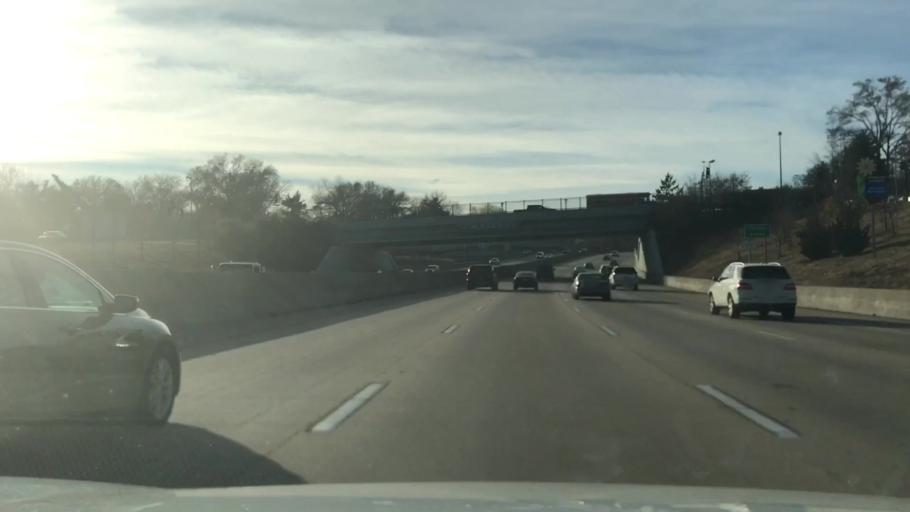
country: US
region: Missouri
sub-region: Saint Louis County
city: Brentwood
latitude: 38.6307
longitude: -90.3611
